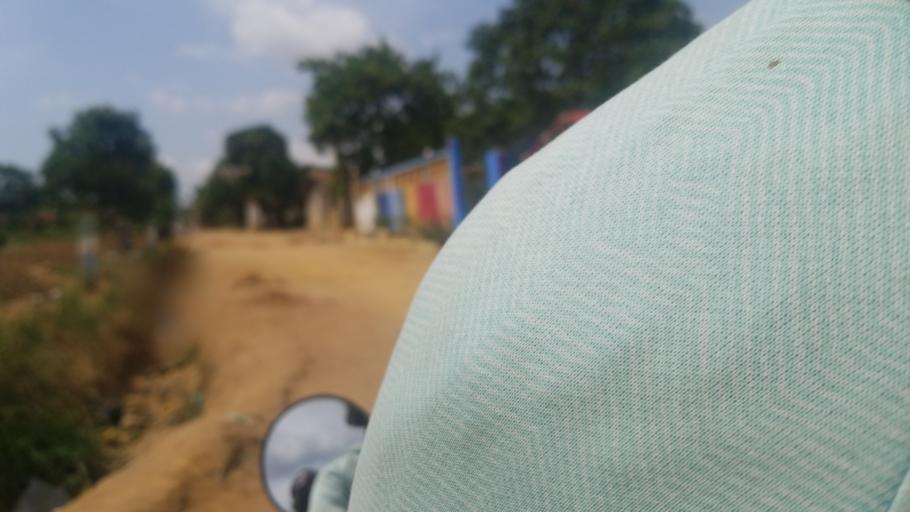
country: SL
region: Western Area
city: Waterloo
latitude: 8.3148
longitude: -13.0463
